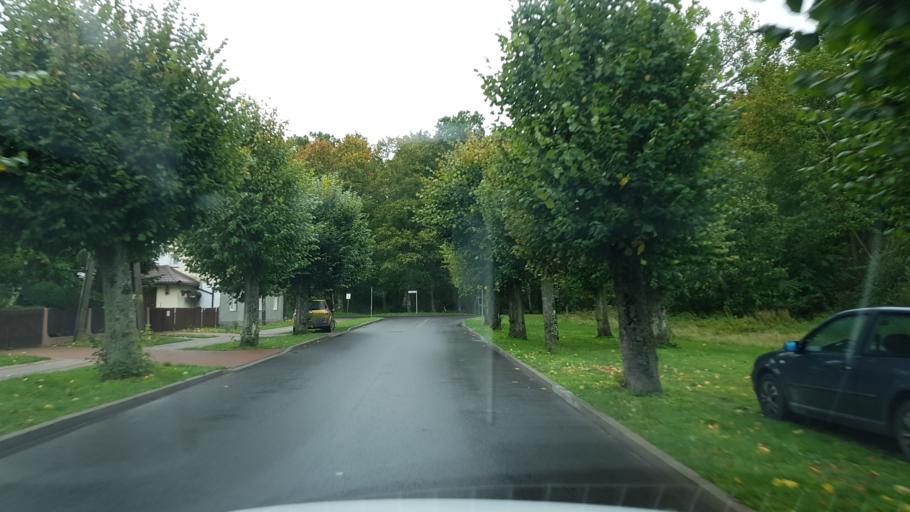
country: PL
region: West Pomeranian Voivodeship
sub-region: Powiat kamienski
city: Wolin
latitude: 53.8353
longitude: 14.6078
